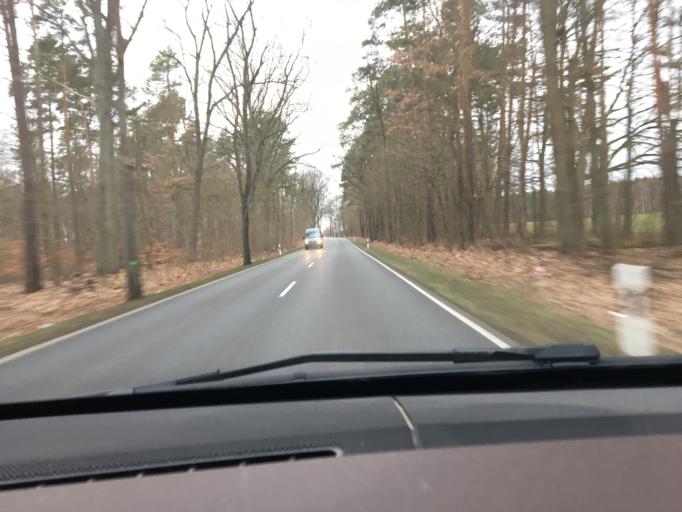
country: DE
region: Brandenburg
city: Liebenwalde
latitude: 52.8756
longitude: 13.4791
